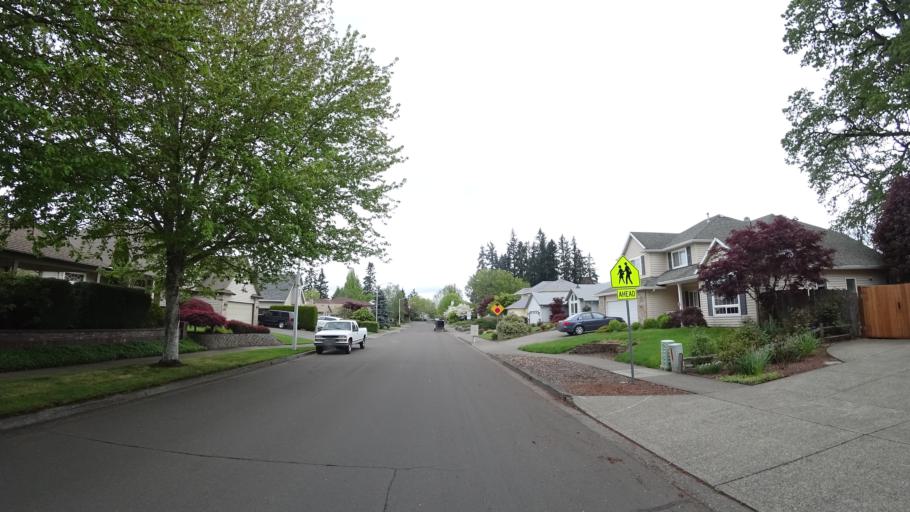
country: US
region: Oregon
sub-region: Washington County
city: Hillsboro
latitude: 45.5433
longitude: -122.9829
